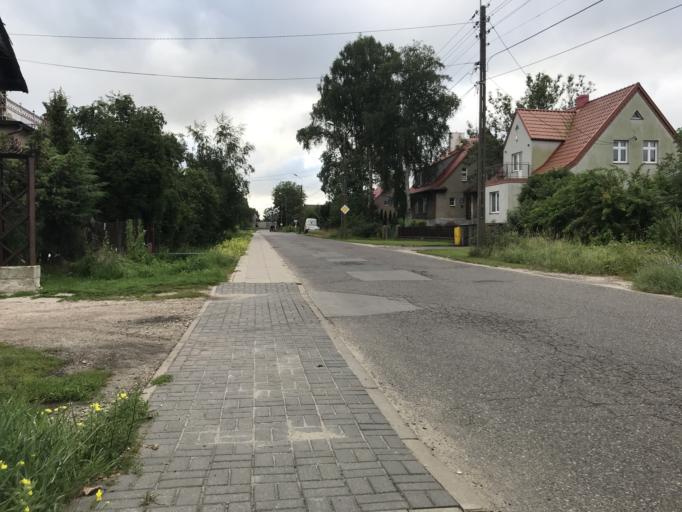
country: PL
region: Pomeranian Voivodeship
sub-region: Gdansk
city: Gdansk
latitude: 54.3388
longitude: 18.6732
